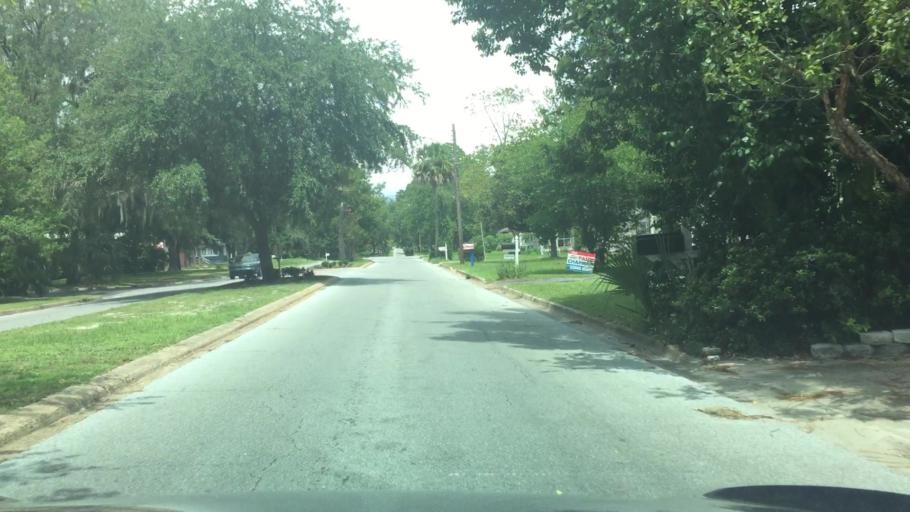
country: US
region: Florida
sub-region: Bay County
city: Panama City
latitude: 30.1483
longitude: -85.6504
